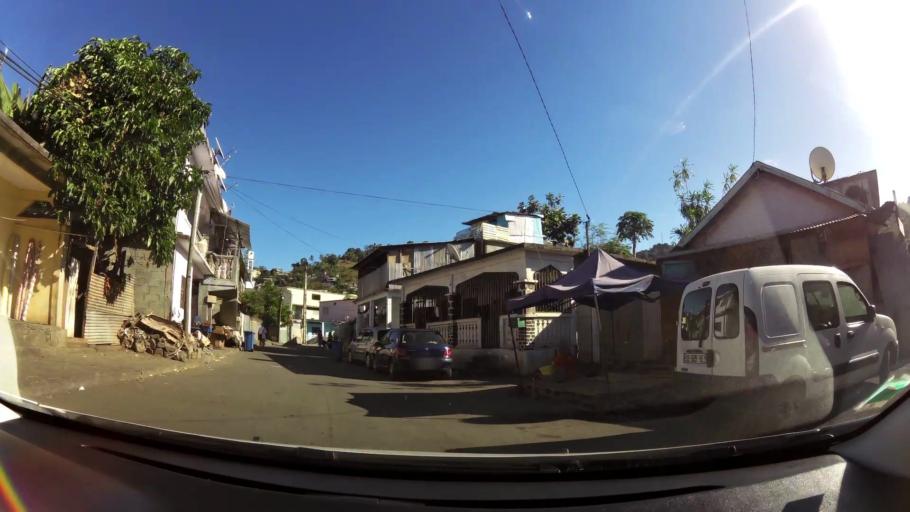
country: YT
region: Mamoudzou
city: Mamoudzou
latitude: -12.7721
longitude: 45.2216
